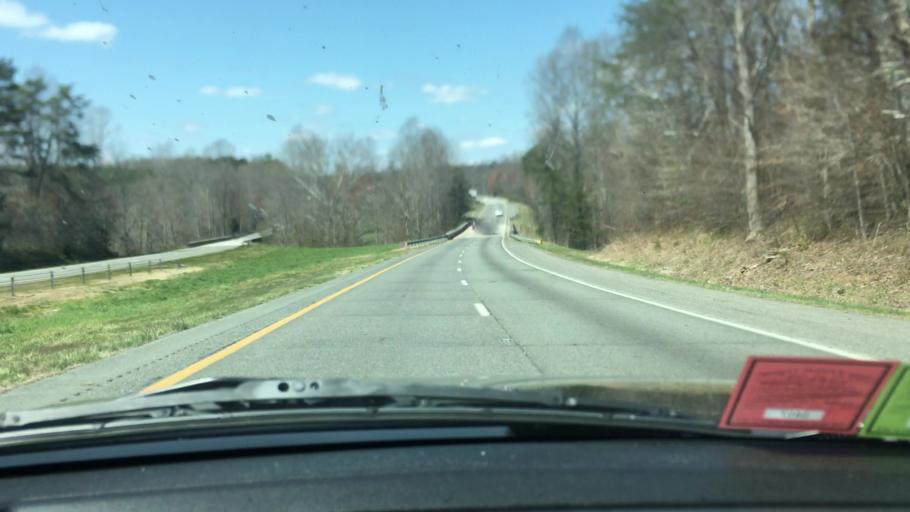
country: US
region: North Carolina
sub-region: Surry County
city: Pilot Mountain
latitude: 36.3958
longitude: -80.4914
